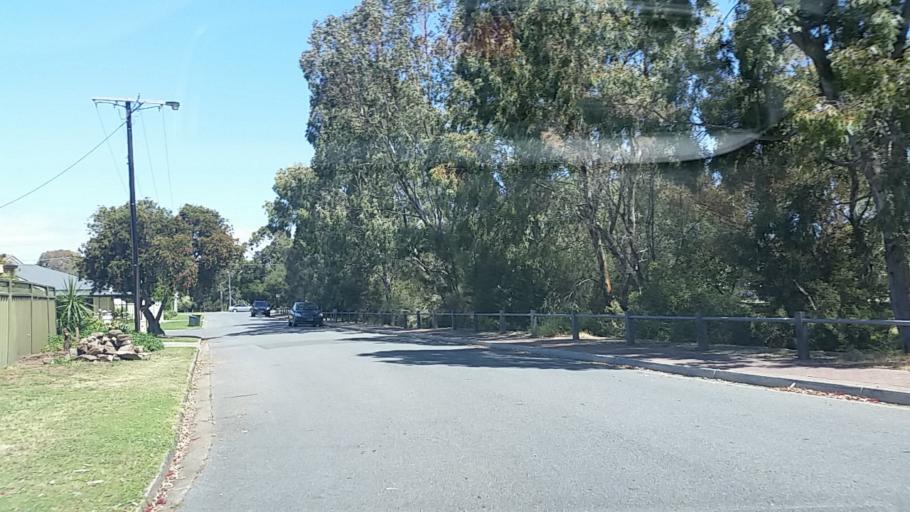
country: AU
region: South Australia
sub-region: Charles Sturt
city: Grange
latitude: -34.9010
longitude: 138.4983
